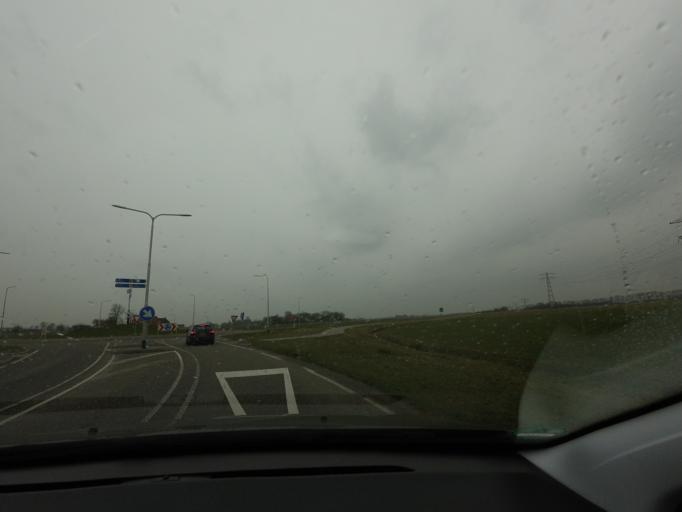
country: NL
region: Friesland
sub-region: Gemeente Franekeradeel
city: Franeker
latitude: 53.1744
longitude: 5.5513
